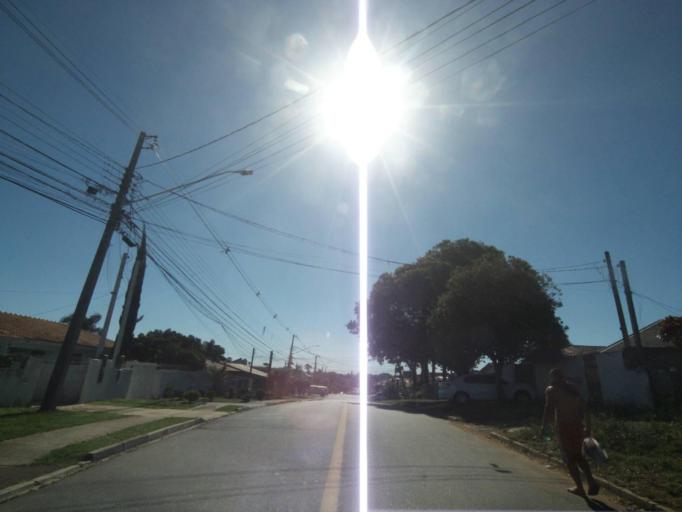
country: BR
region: Parana
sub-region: Curitiba
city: Curitiba
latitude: -25.4552
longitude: -49.3459
